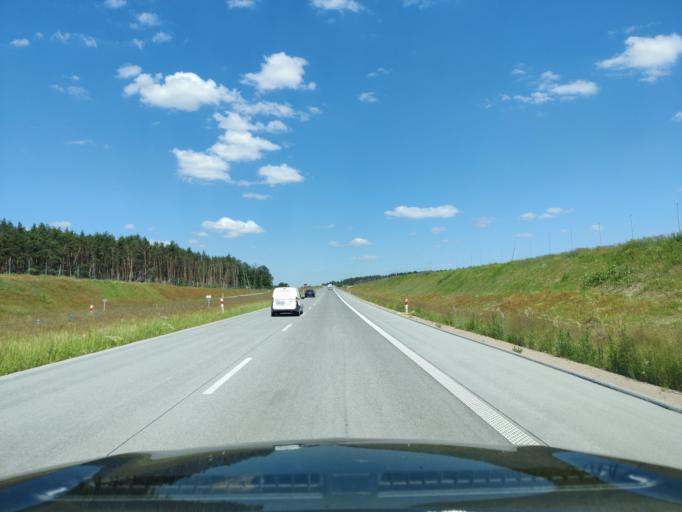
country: PL
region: Masovian Voivodeship
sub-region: Powiat mlawski
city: Strzegowo
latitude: 52.9746
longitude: 20.3282
